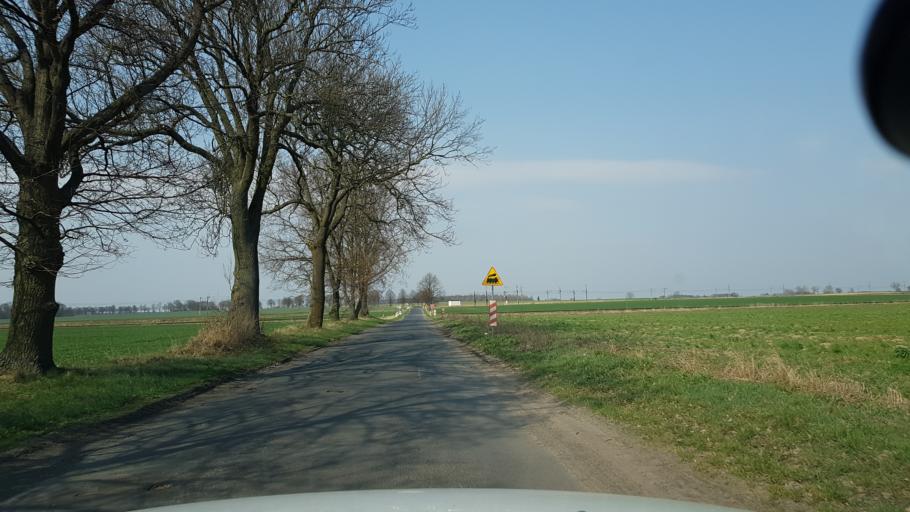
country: PL
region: West Pomeranian Voivodeship
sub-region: Powiat stargardzki
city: Stara Dabrowa
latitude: 53.3511
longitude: 15.1318
